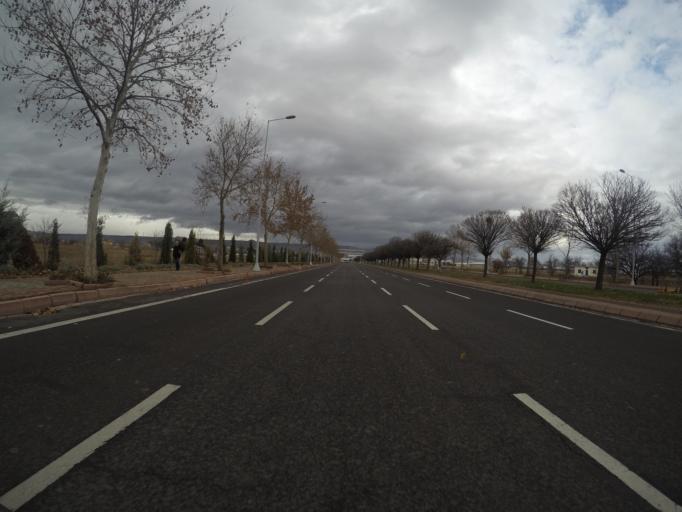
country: TR
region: Kayseri
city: Kayseri
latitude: 38.7600
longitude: 35.4822
